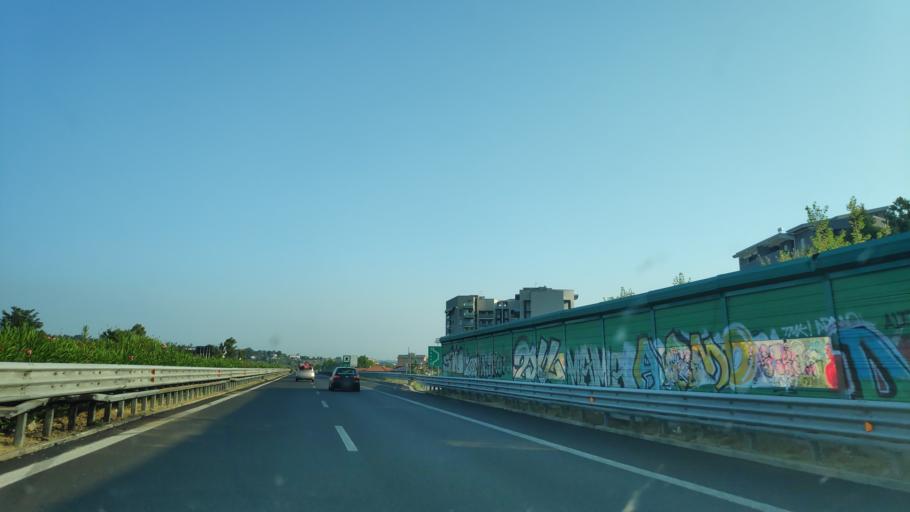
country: IT
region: Calabria
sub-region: Provincia di Cosenza
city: Quattromiglia
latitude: 39.3298
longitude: 16.2389
